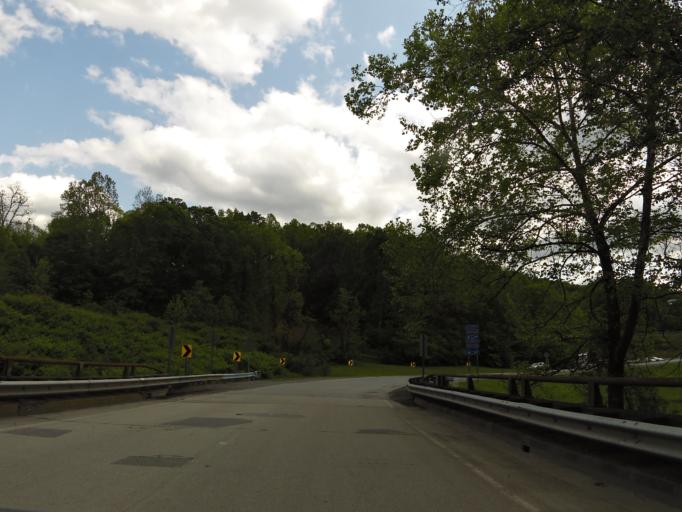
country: US
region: West Virginia
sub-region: Fayette County
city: Oak Hill
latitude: 37.9753
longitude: -81.2837
